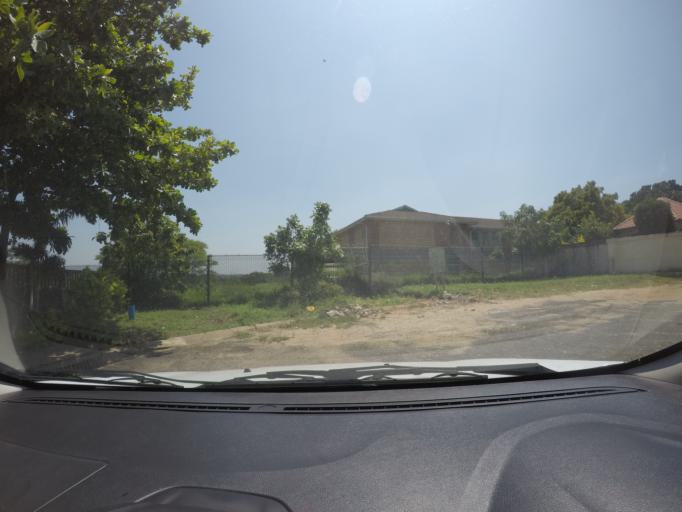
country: ZA
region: KwaZulu-Natal
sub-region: uThungulu District Municipality
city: eSikhawini
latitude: -28.8683
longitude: 31.9210
